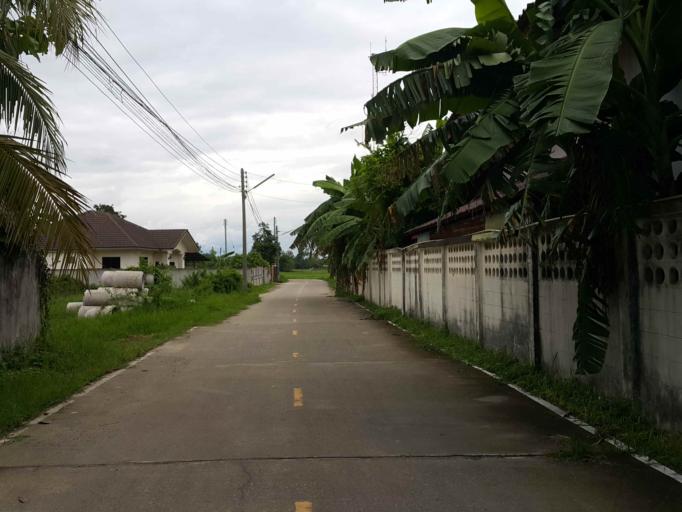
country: TH
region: Chiang Mai
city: San Sai
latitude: 18.8205
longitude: 99.0754
